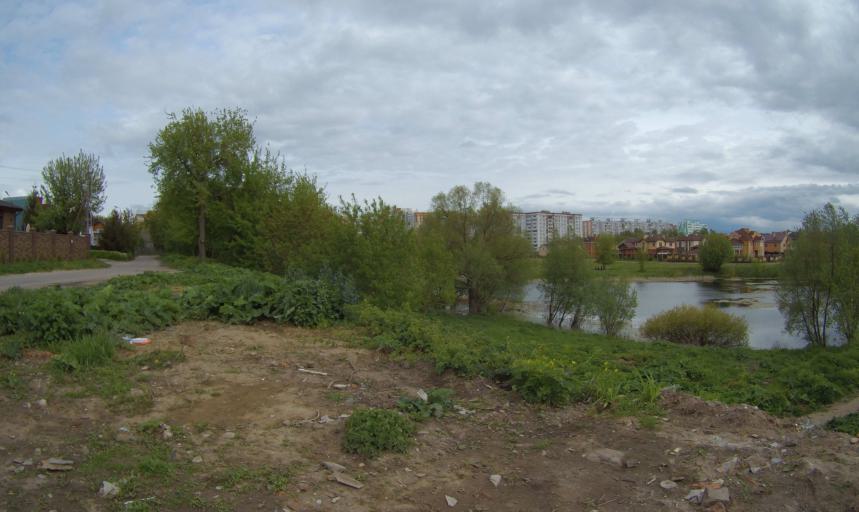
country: RU
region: Moskovskaya
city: Kolomna
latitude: 55.0963
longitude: 38.7535
